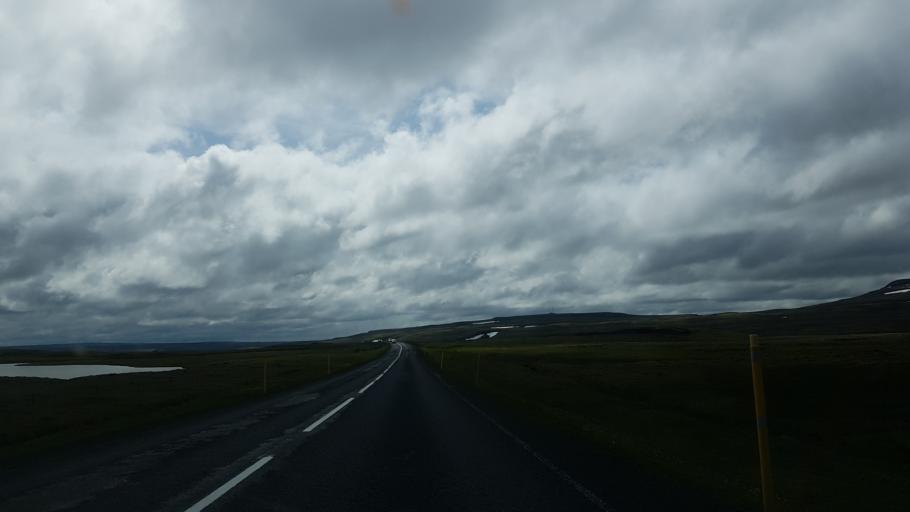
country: IS
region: West
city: Borgarnes
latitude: 64.9807
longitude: -21.0606
